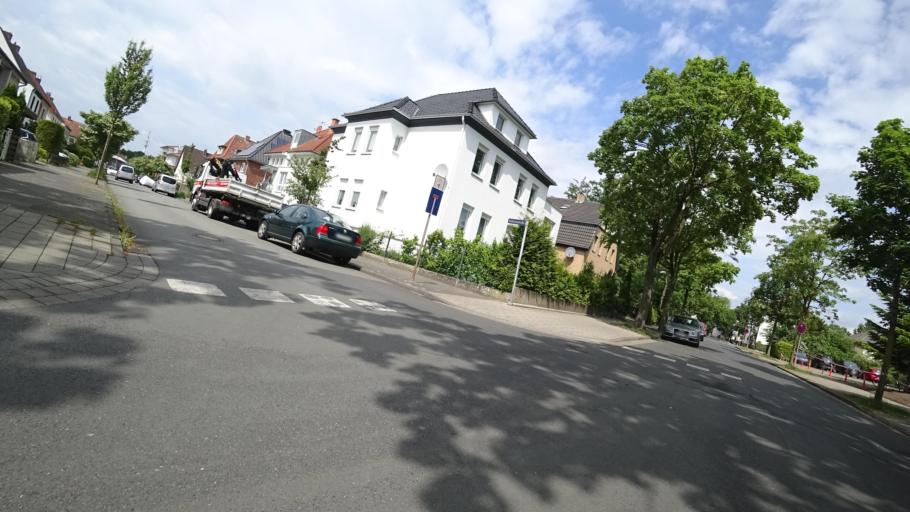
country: DE
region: North Rhine-Westphalia
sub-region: Regierungsbezirk Detmold
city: Guetersloh
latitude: 51.9061
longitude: 8.3954
